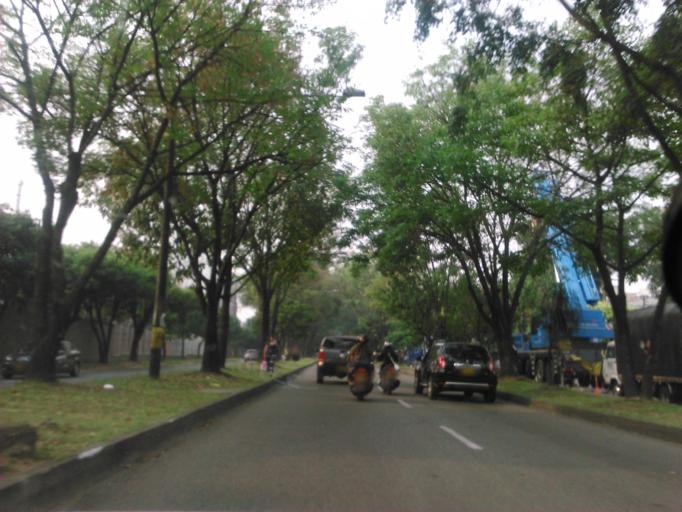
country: CO
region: Antioquia
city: Itagui
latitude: 6.2003
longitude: -75.5846
